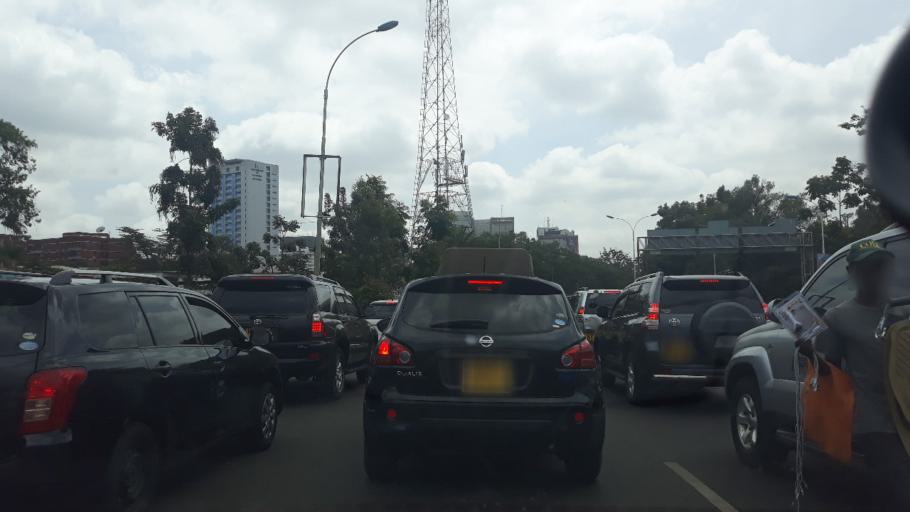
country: KE
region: Nairobi Area
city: Nairobi
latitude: -1.2760
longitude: 36.8133
